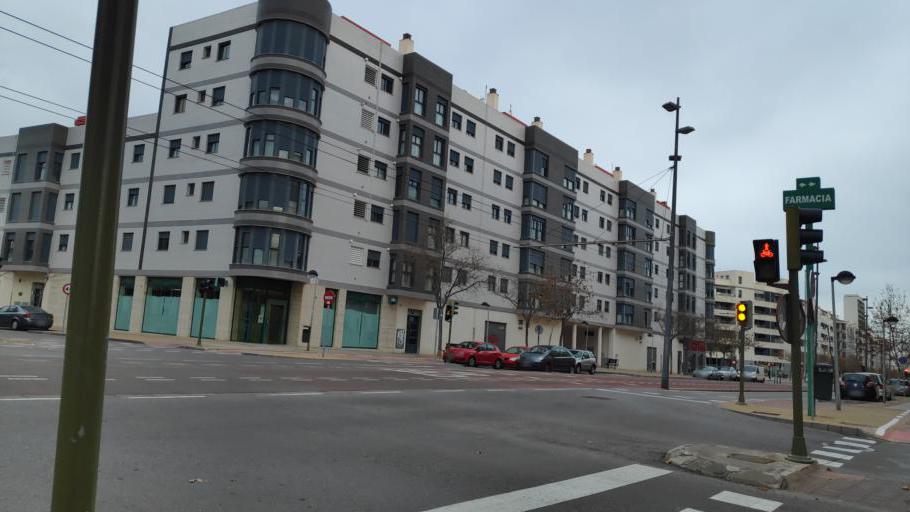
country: ES
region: Valencia
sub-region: Provincia de Castello
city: Castello de la Plana
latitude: 39.9920
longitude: -0.0621
